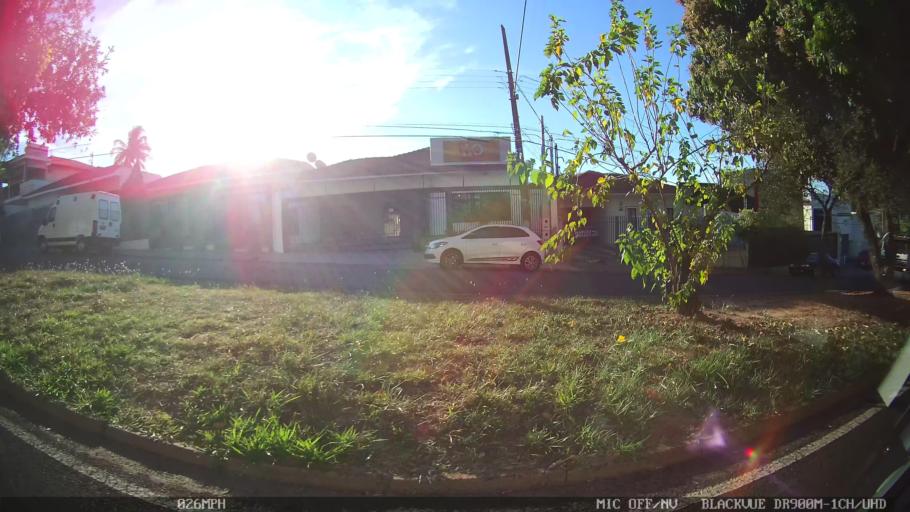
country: BR
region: Sao Paulo
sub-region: Sao Jose Do Rio Preto
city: Sao Jose do Rio Preto
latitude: -20.8293
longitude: -49.3668
